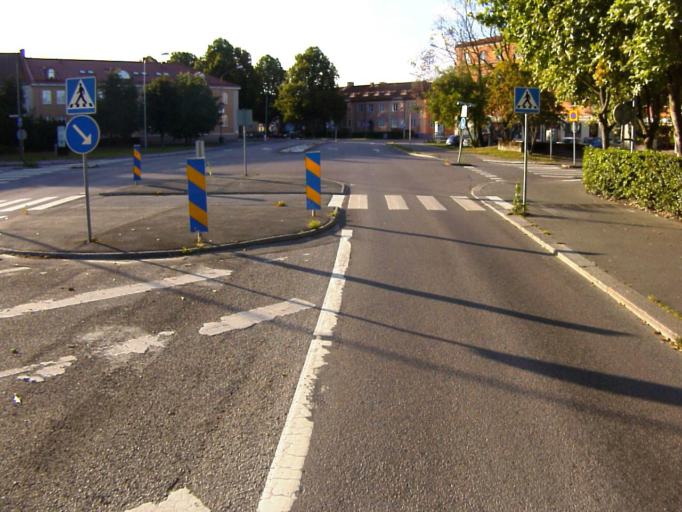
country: SE
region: Soedermanland
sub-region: Eskilstuna Kommun
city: Eskilstuna
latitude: 59.3720
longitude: 16.5210
